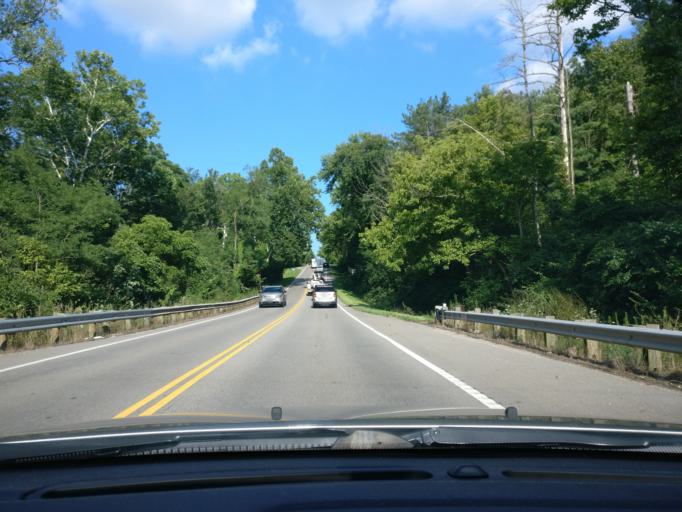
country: US
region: Ohio
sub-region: Warren County
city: Five Points
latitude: 39.5458
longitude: -84.1845
